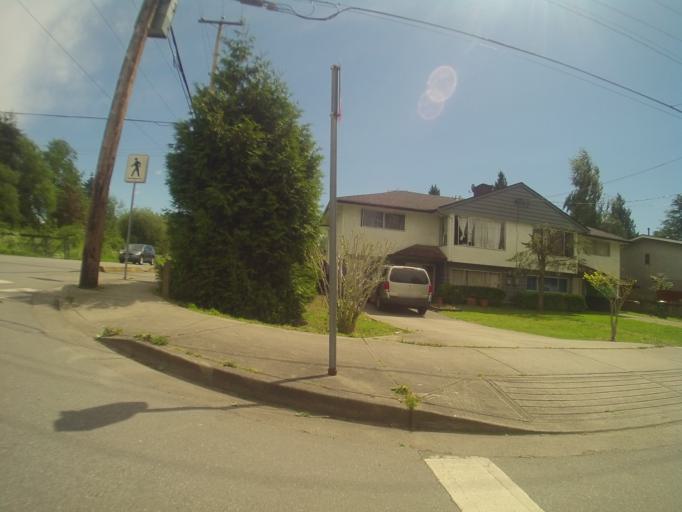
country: CA
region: British Columbia
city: Richmond
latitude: 49.1898
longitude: -123.1028
